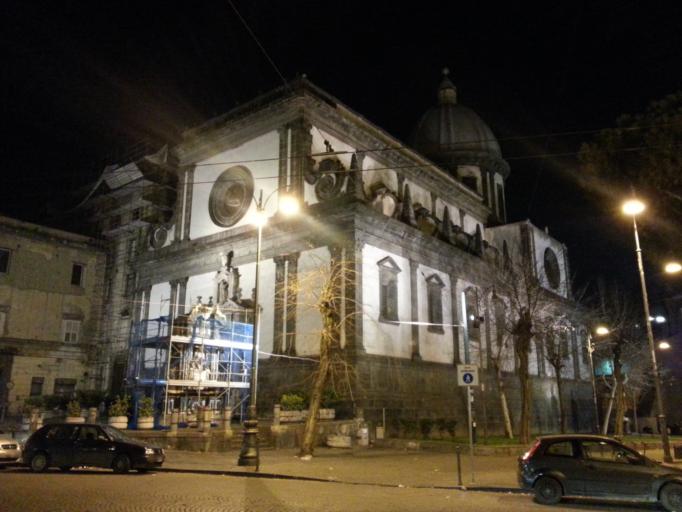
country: IT
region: Campania
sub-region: Provincia di Napoli
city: Napoli
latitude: 40.8540
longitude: 14.2647
